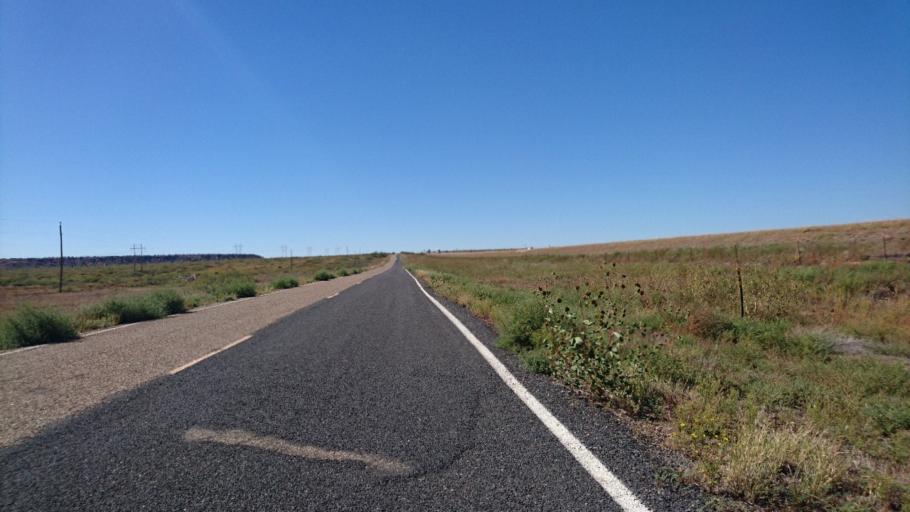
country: US
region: New Mexico
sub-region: Quay County
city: Tucumcari
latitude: 35.0832
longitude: -104.1100
